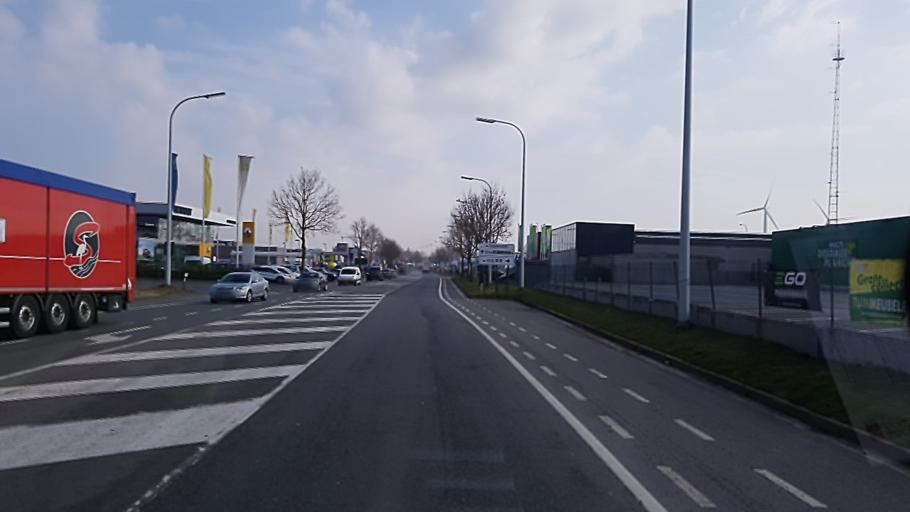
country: BE
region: Flanders
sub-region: Provincie West-Vlaanderen
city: Poperinge
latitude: 50.8485
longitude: 2.7392
